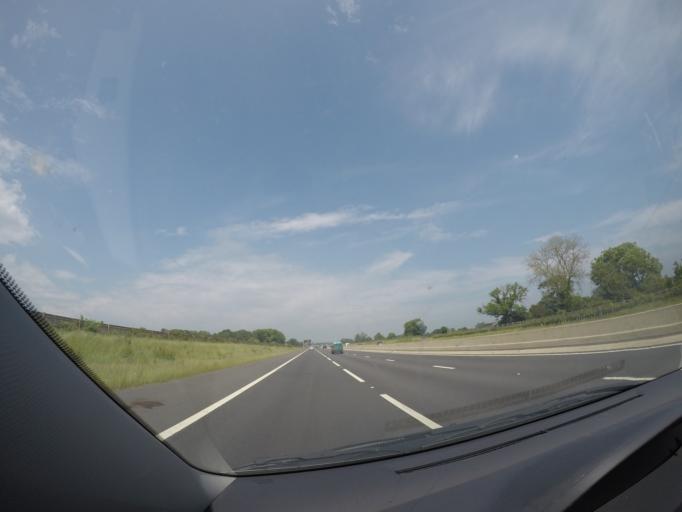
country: GB
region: England
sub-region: North Yorkshire
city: Catterick
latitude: 54.4240
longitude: -1.6653
